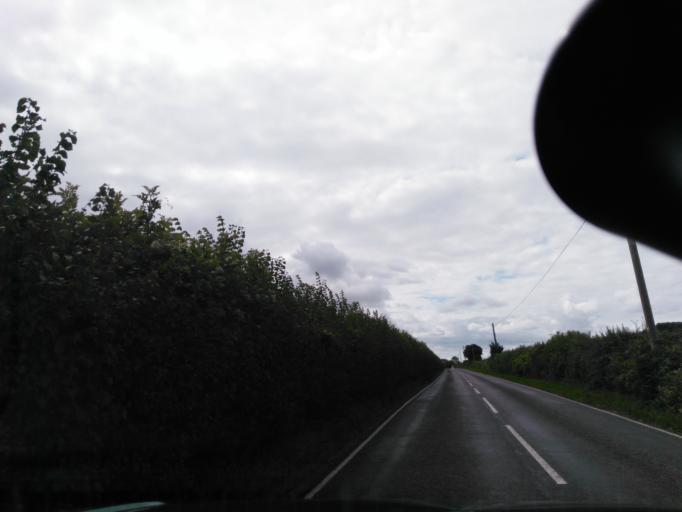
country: GB
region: England
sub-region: Dorset
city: Blandford Forum
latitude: 50.8954
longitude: -2.1563
